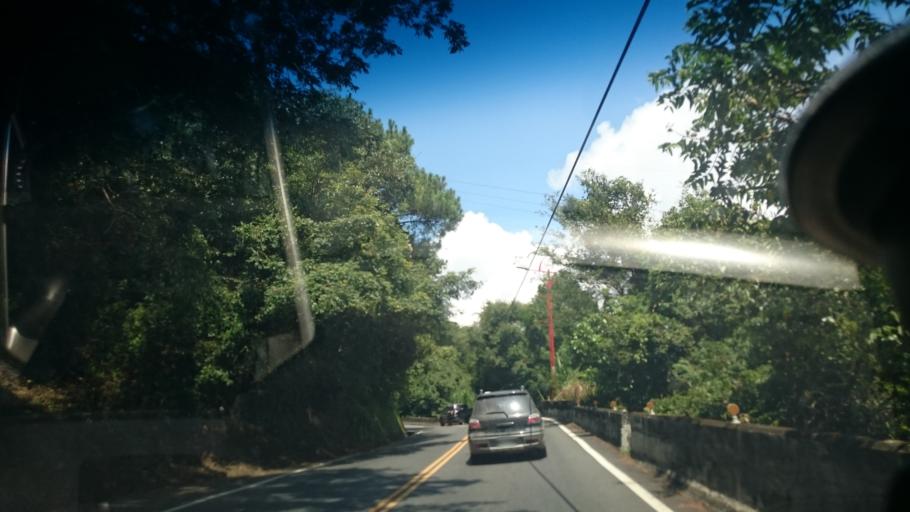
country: TW
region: Taiwan
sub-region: Nantou
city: Puli
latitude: 24.0262
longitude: 121.1410
